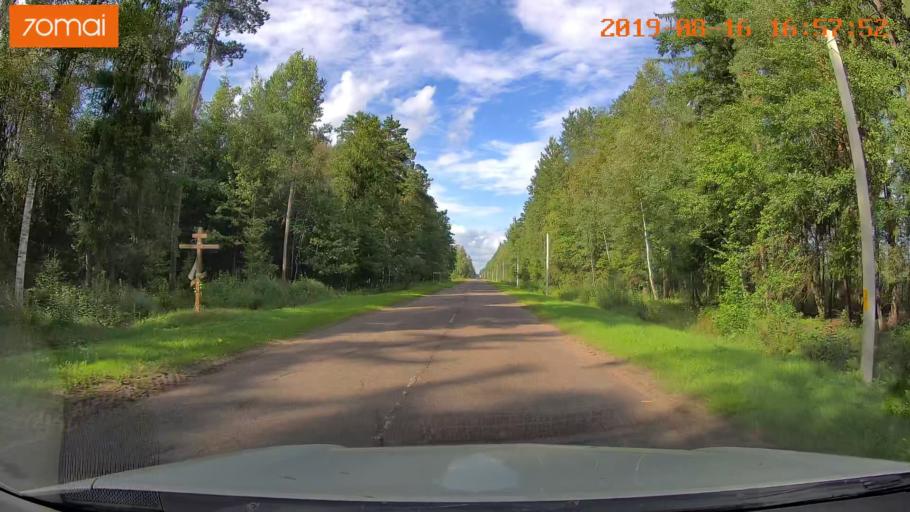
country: BY
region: Mogilev
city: Hlusha
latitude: 53.2617
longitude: 28.8282
